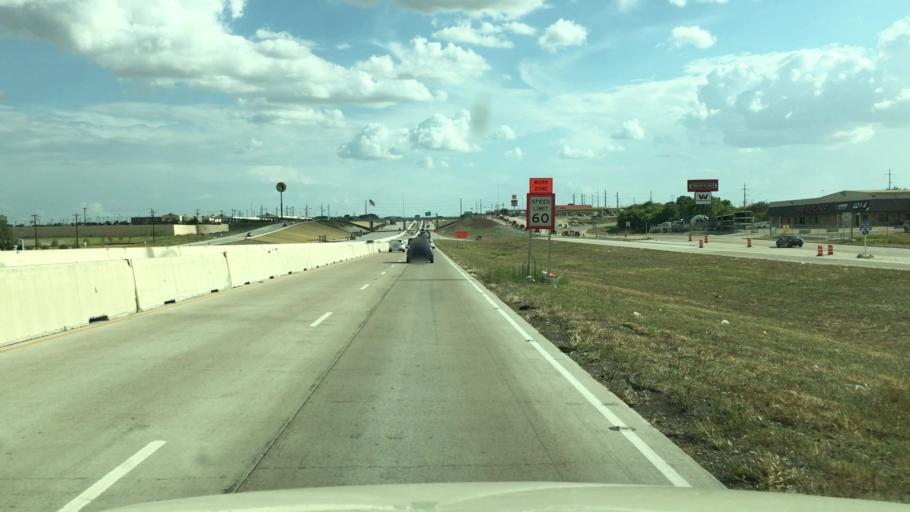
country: US
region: Texas
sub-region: Bell County
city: Temple
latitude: 31.1445
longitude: -97.3280
